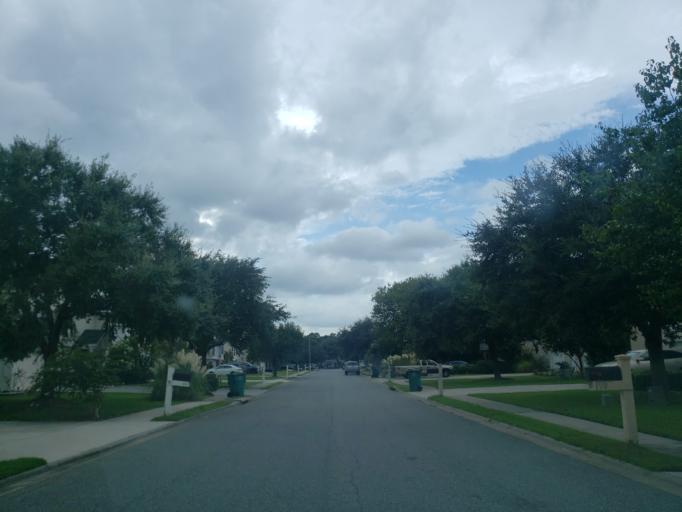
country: US
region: Georgia
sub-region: Chatham County
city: Wilmington Island
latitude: 32.0232
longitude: -80.9566
